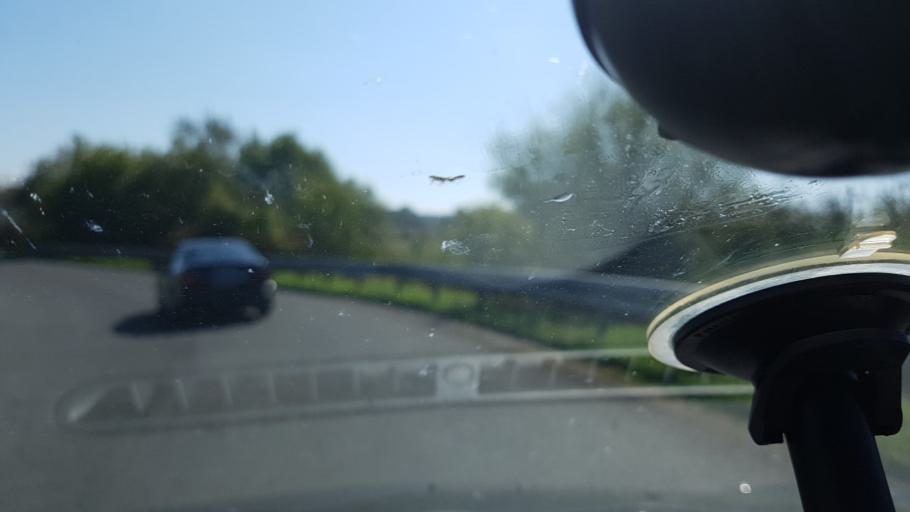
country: HR
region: Zagrebacka
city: Lupoglav
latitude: 45.7505
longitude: 16.2960
